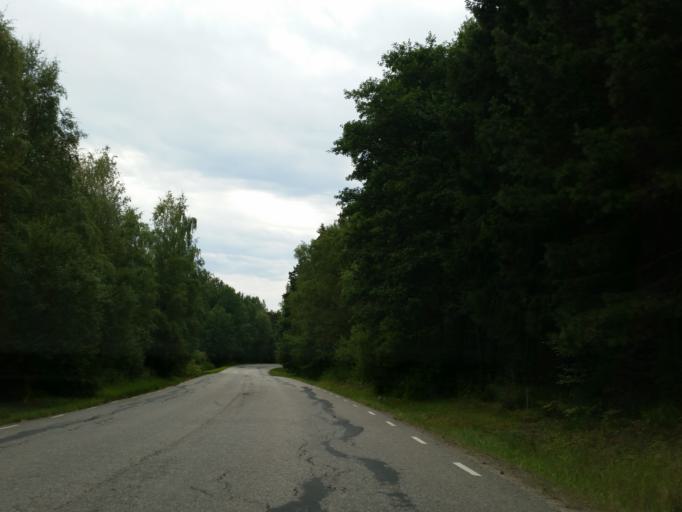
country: SE
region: Stockholm
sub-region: Sodertalje Kommun
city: Soedertaelje
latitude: 59.2110
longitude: 17.6524
